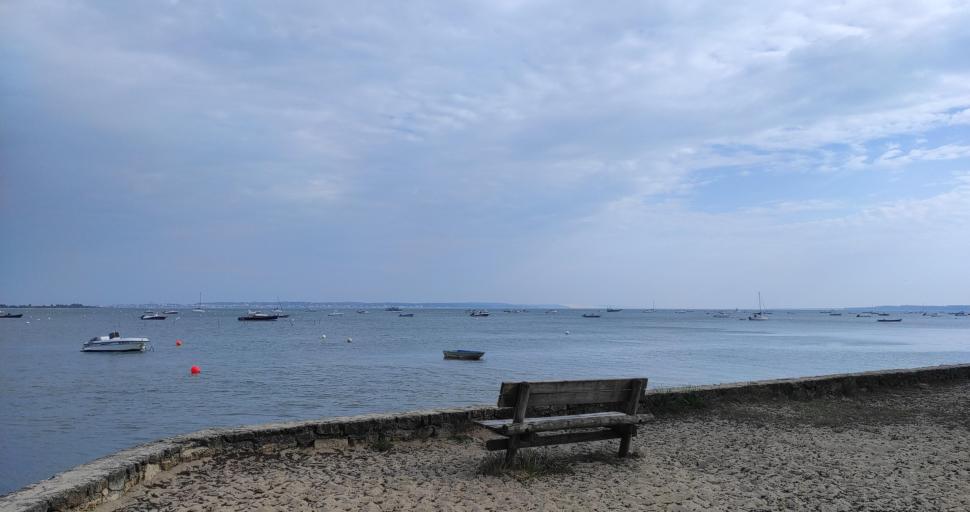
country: FR
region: Aquitaine
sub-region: Departement de la Gironde
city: Arcachon
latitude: 44.7178
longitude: -1.2046
